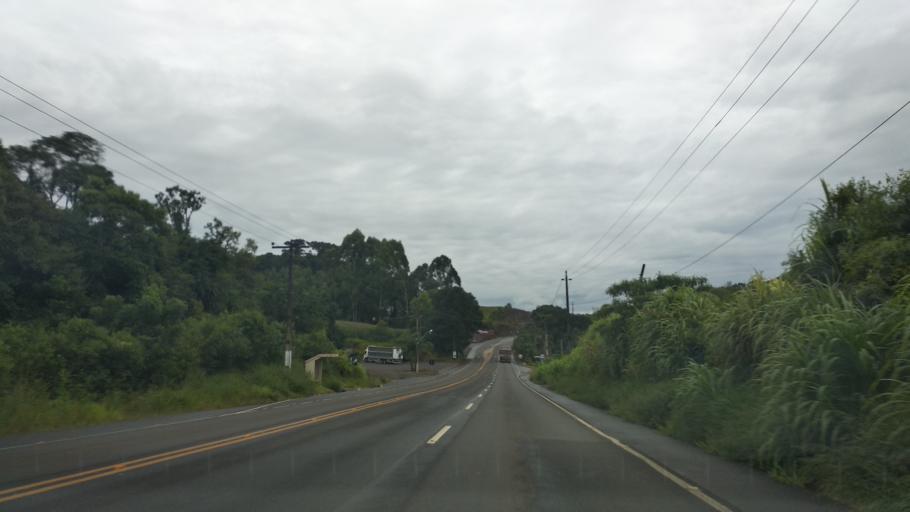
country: BR
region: Santa Catarina
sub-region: Videira
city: Videira
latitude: -27.0355
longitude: -51.1543
